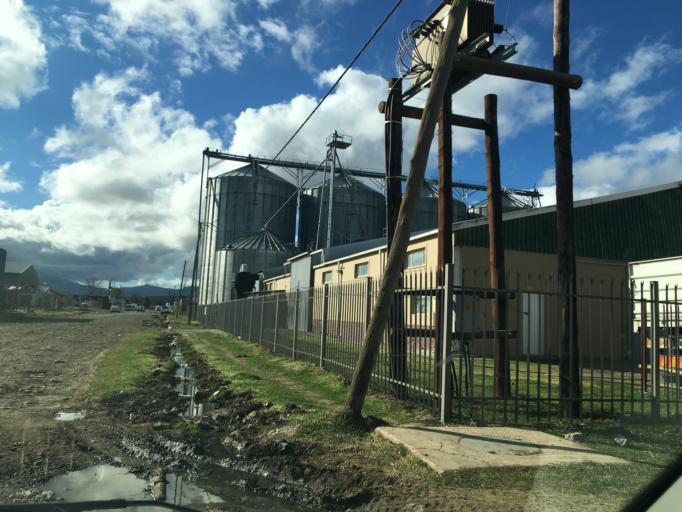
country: ZA
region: Eastern Cape
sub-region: Chris Hani District Municipality
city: Elliot
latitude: -31.3370
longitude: 27.8471
